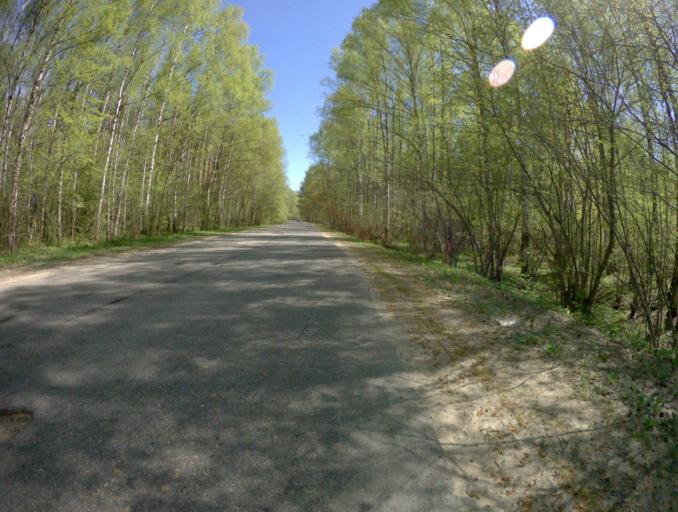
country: RU
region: Vladimir
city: Orgtrud
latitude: 56.1987
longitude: 40.5896
